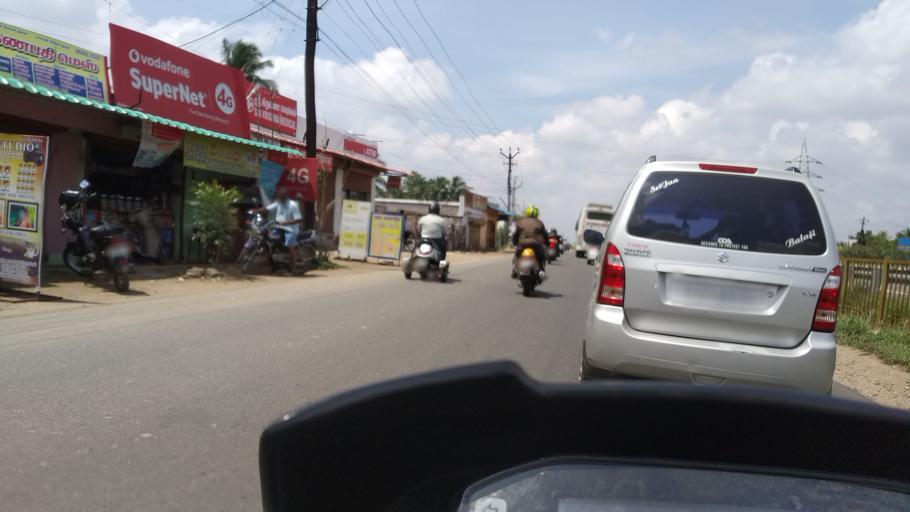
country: IN
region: Tamil Nadu
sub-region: Coimbatore
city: Sulur
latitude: 11.0916
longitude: 77.1408
